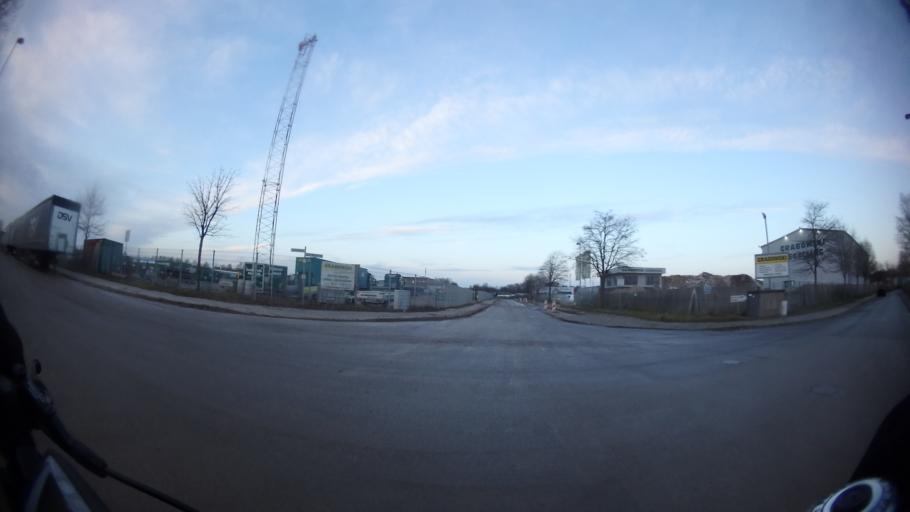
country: DE
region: Mecklenburg-Vorpommern
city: Selmsdorf
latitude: 53.9002
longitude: 10.8126
